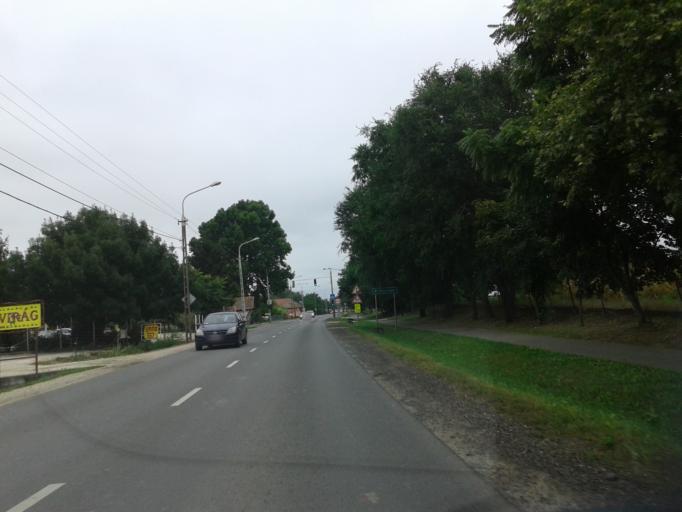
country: HU
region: Bacs-Kiskun
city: Solt
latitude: 46.7998
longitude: 19.0276
